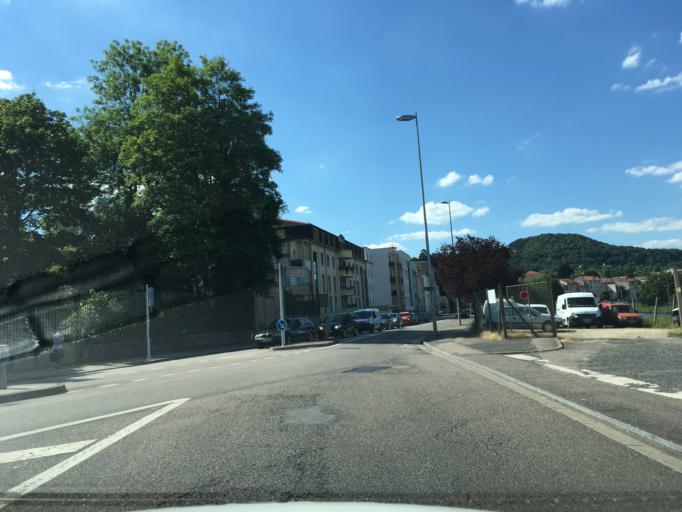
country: FR
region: Lorraine
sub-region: Departement de Meurthe-et-Moselle
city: Maxeville
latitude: 48.7048
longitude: 6.1695
